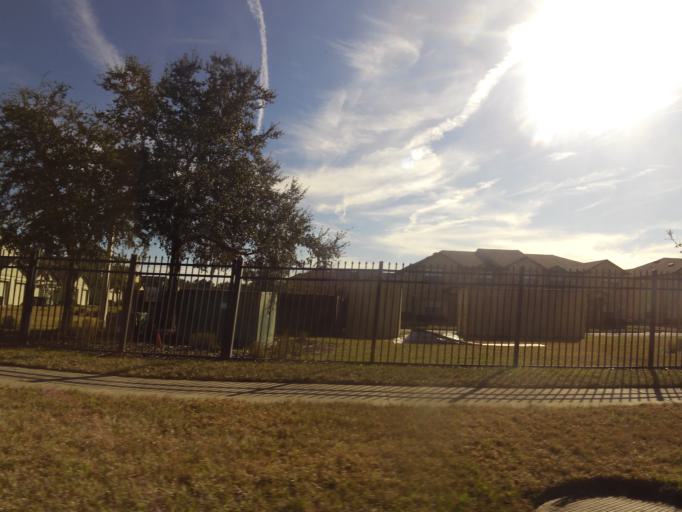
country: US
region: Florida
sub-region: Saint Johns County
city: Saint Augustine
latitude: 29.9250
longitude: -81.4080
